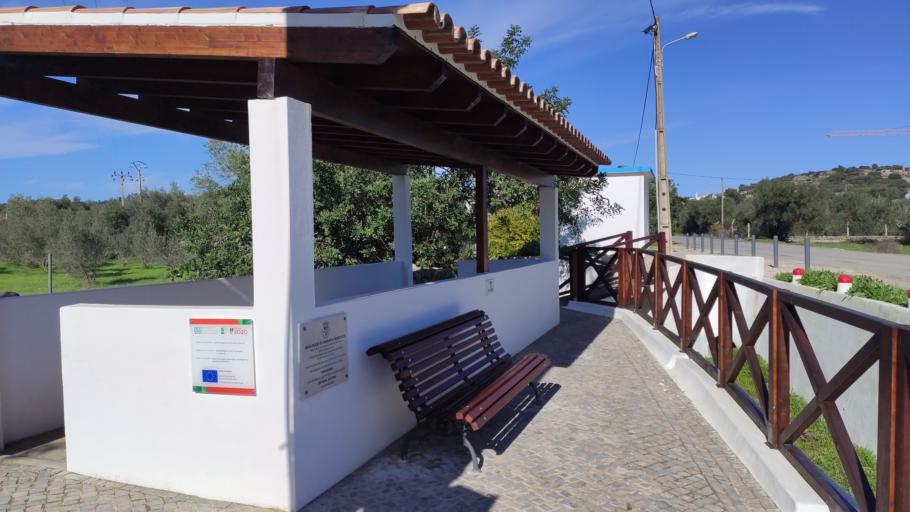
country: PT
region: Faro
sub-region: Sao Bras de Alportel
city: Sao Bras de Alportel
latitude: 37.1529
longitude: -7.8562
